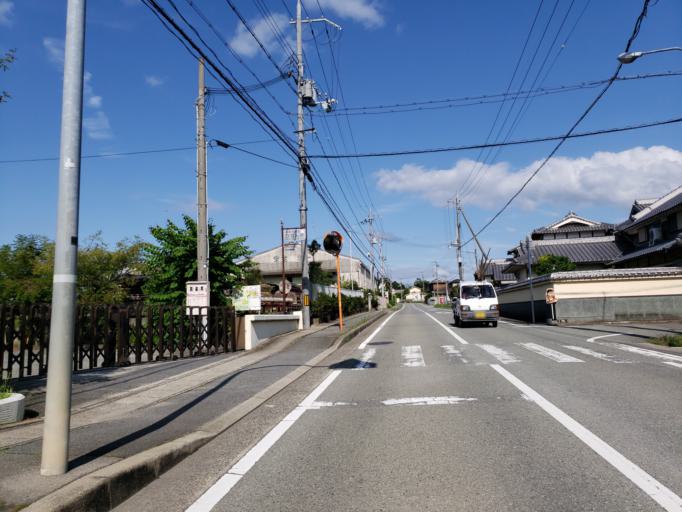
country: JP
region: Hyogo
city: Himeji
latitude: 34.9111
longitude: 134.7582
